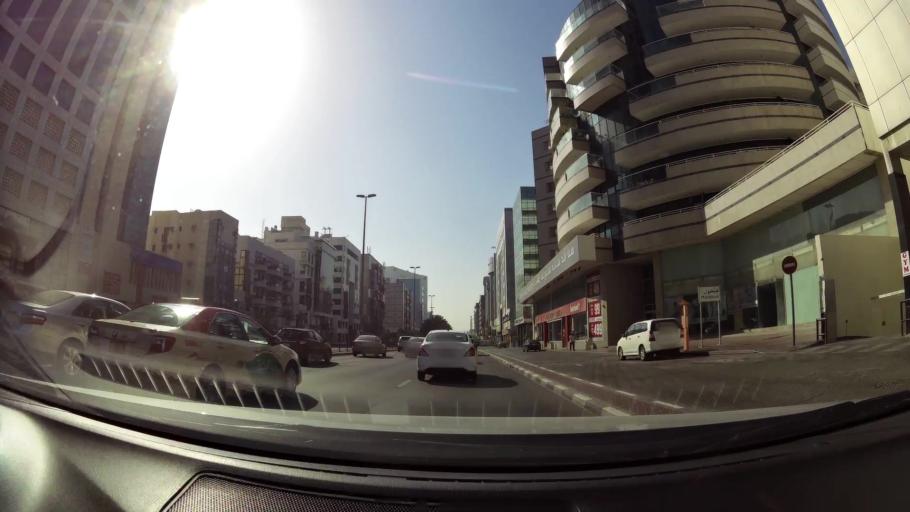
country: AE
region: Ash Shariqah
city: Sharjah
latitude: 25.2578
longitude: 55.2981
